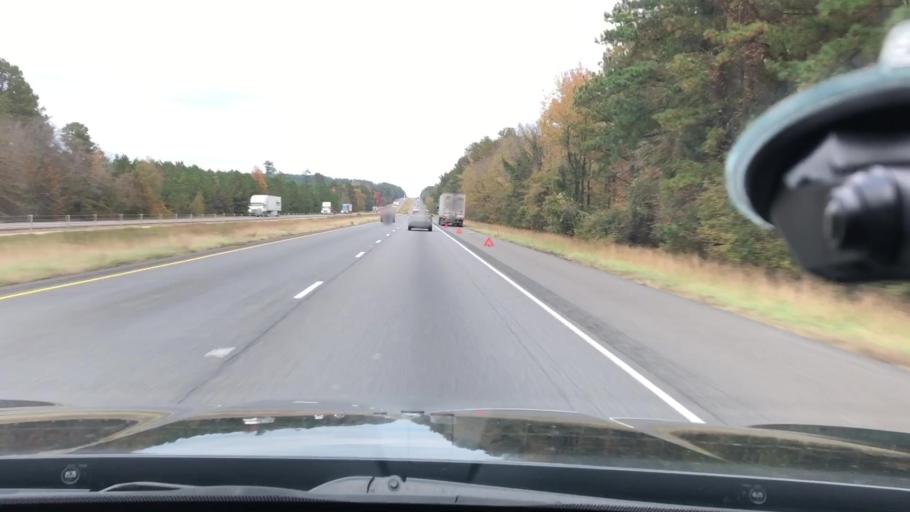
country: US
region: Arkansas
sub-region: Clark County
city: Arkadelphia
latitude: 34.2590
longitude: -92.9828
